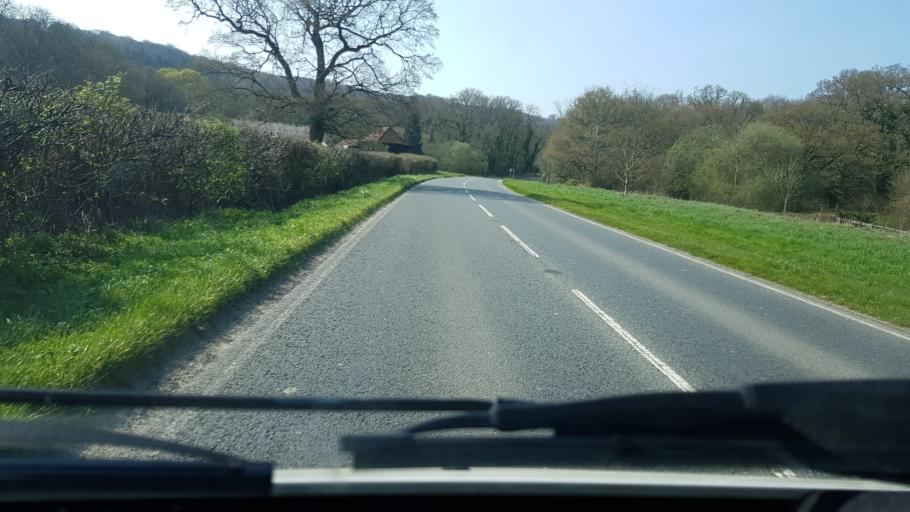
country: GB
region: England
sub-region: West Sussex
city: Fernhurst
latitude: 51.0327
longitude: -0.7282
